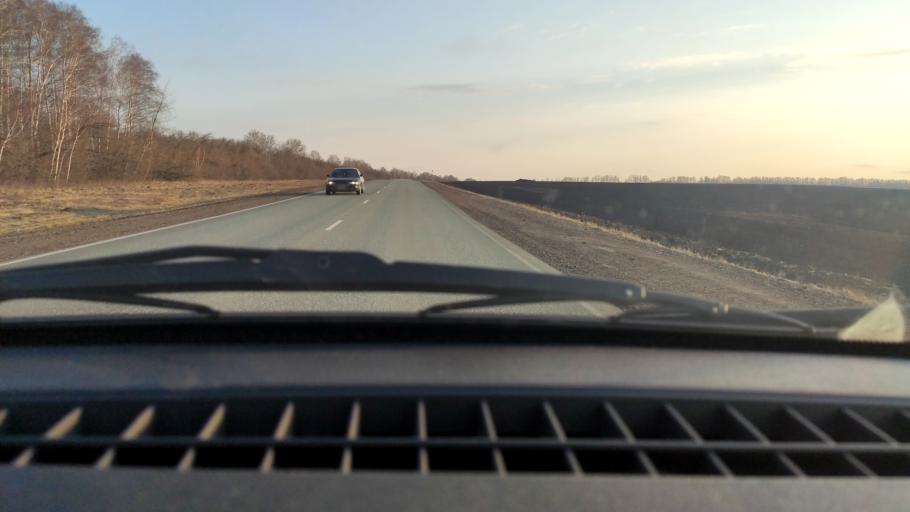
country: RU
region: Bashkortostan
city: Chishmy
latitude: 54.5091
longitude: 55.2908
